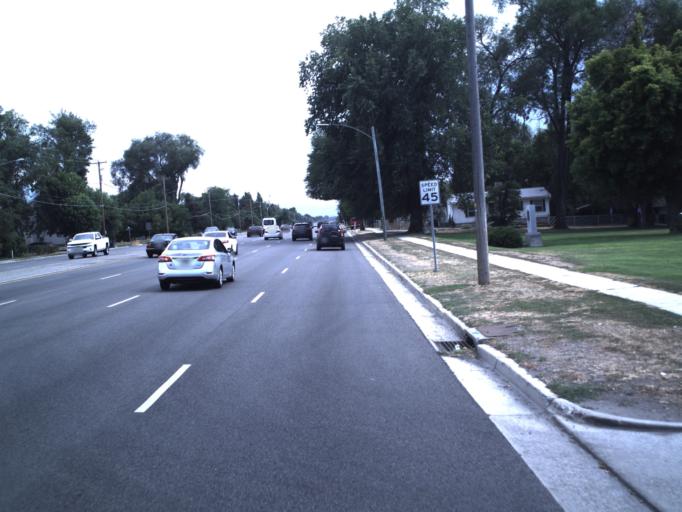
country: US
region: Utah
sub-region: Salt Lake County
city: South Salt Lake
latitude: 40.7103
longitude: -111.8715
